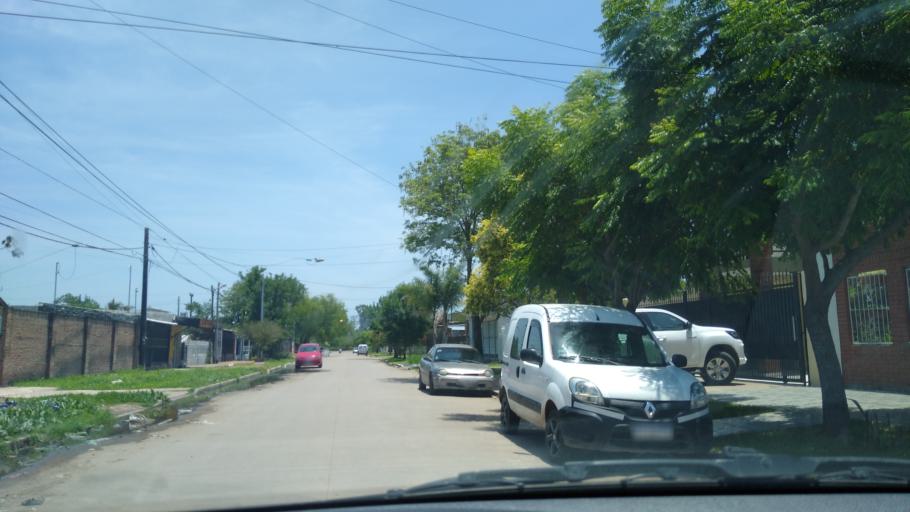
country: AR
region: Chaco
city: Barranqueras
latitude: -27.4861
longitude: -58.9505
